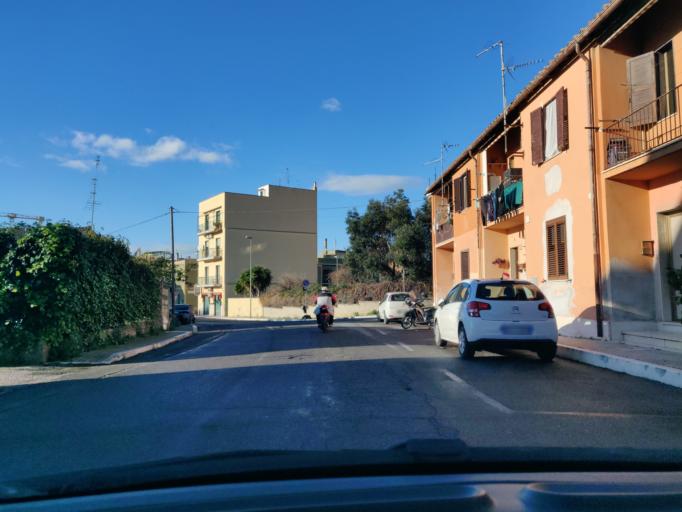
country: IT
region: Latium
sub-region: Citta metropolitana di Roma Capitale
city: Civitavecchia
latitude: 42.0989
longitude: 11.7941
